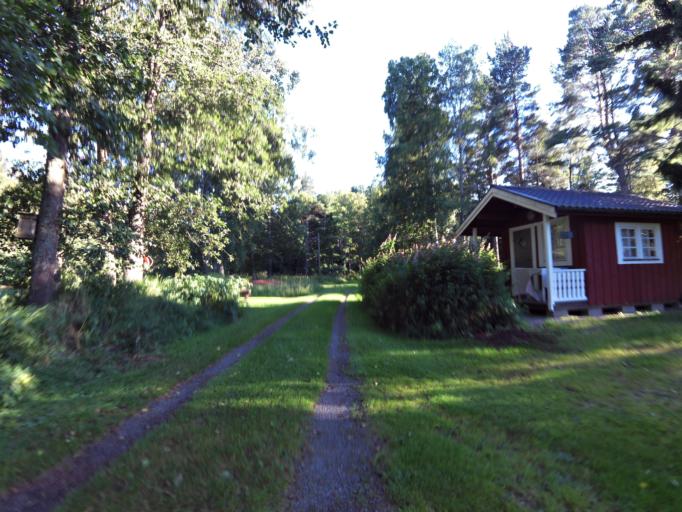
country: SE
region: Gaevleborg
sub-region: Gavle Kommun
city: Gavle
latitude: 60.7093
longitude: 17.1529
